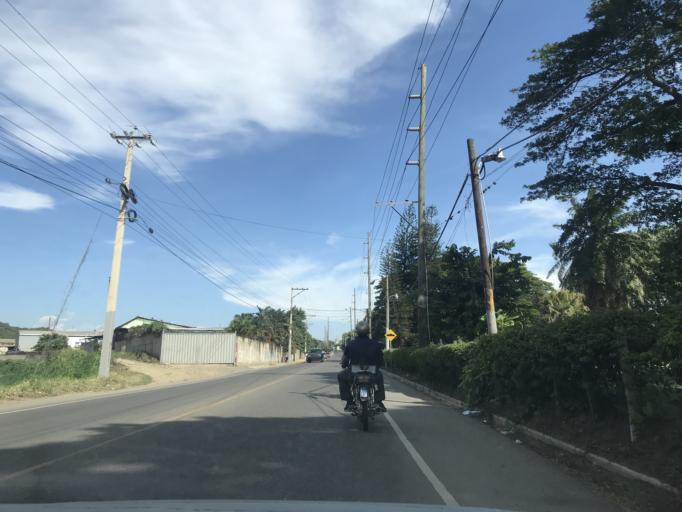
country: DO
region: Santiago
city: Santiago de los Caballeros
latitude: 19.4518
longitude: -70.7454
